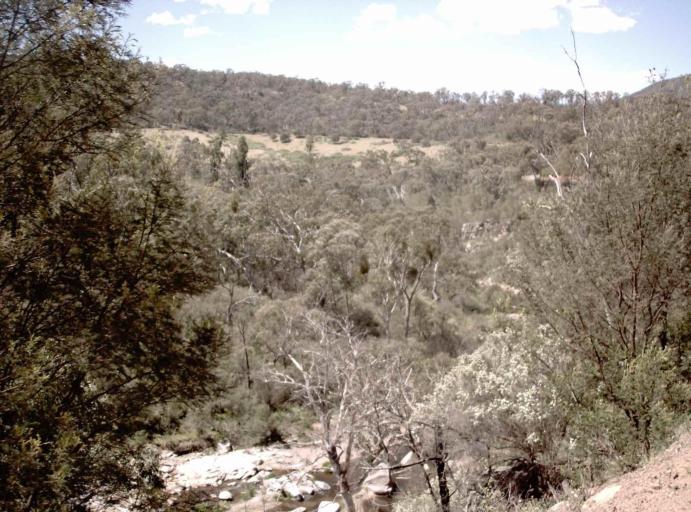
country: AU
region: New South Wales
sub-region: Snowy River
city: Jindabyne
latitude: -37.0371
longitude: 148.5392
